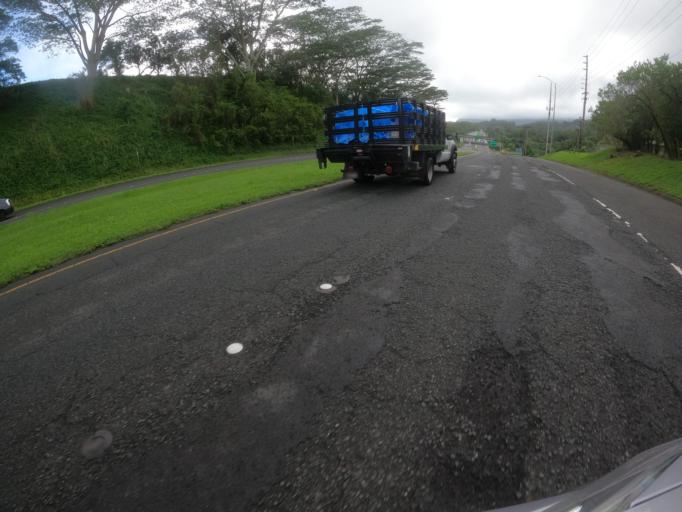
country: US
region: Hawaii
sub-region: Honolulu County
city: Kane'ohe
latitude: 21.3875
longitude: -157.7935
